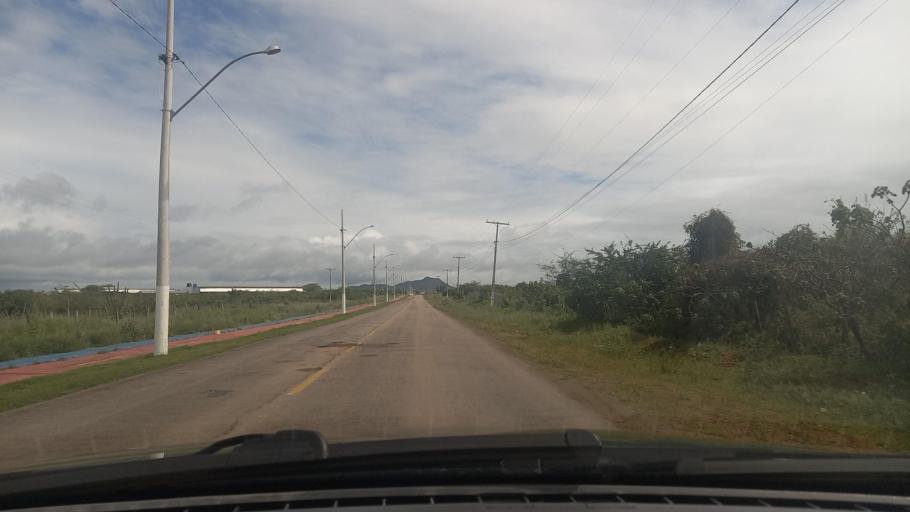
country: BR
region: Bahia
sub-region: Paulo Afonso
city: Paulo Afonso
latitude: -9.3541
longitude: -38.2665
